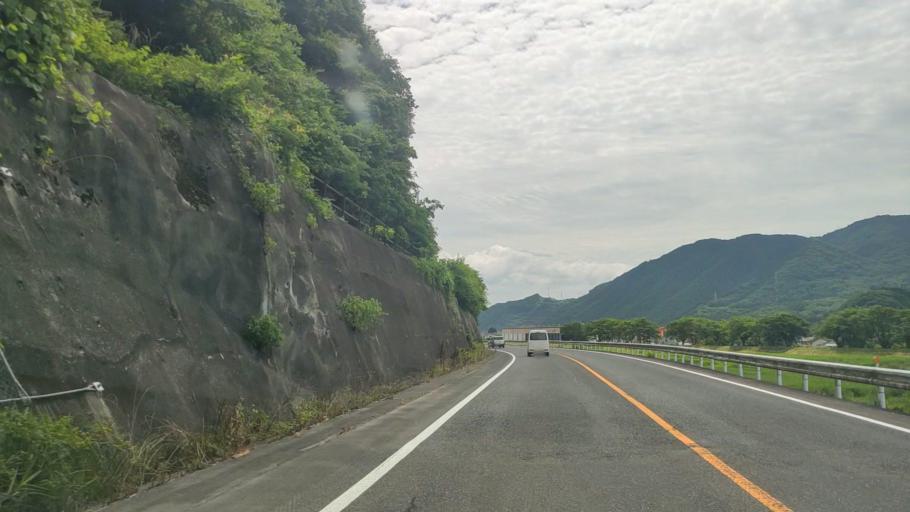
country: JP
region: Okayama
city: Niimi
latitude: 35.0834
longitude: 133.7103
